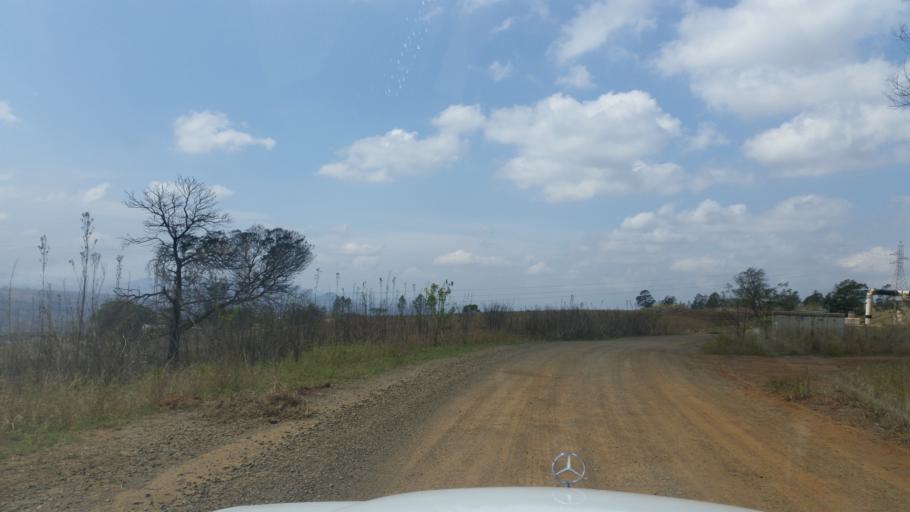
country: ZA
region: KwaZulu-Natal
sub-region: uMgungundlovu District Municipality
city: Camperdown
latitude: -29.7130
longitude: 30.4981
